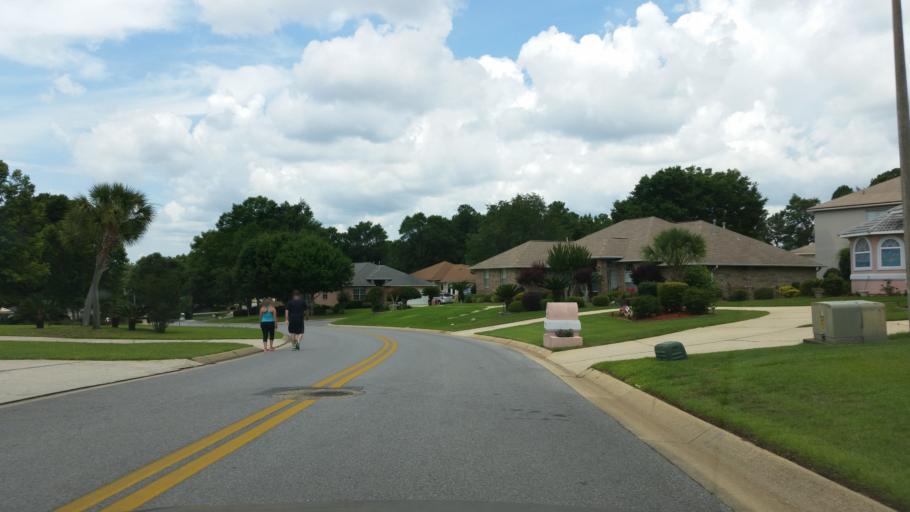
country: US
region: Florida
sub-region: Escambia County
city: Ensley
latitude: 30.4801
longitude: -87.2782
